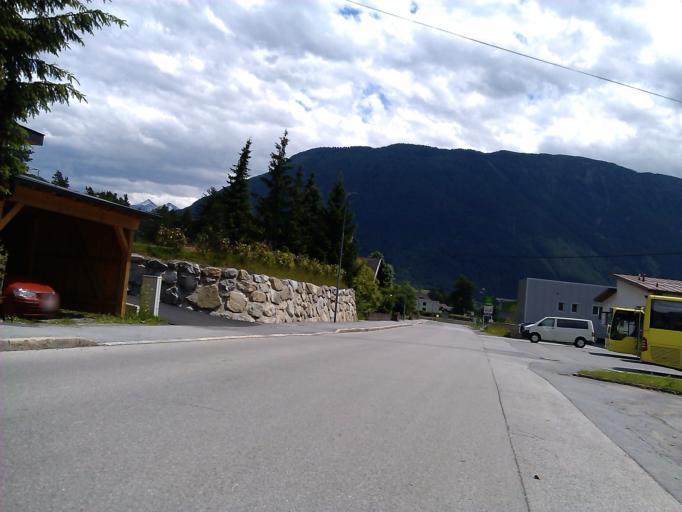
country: AT
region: Tyrol
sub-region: Politischer Bezirk Imst
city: Nassereith
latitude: 47.3186
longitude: 10.8312
